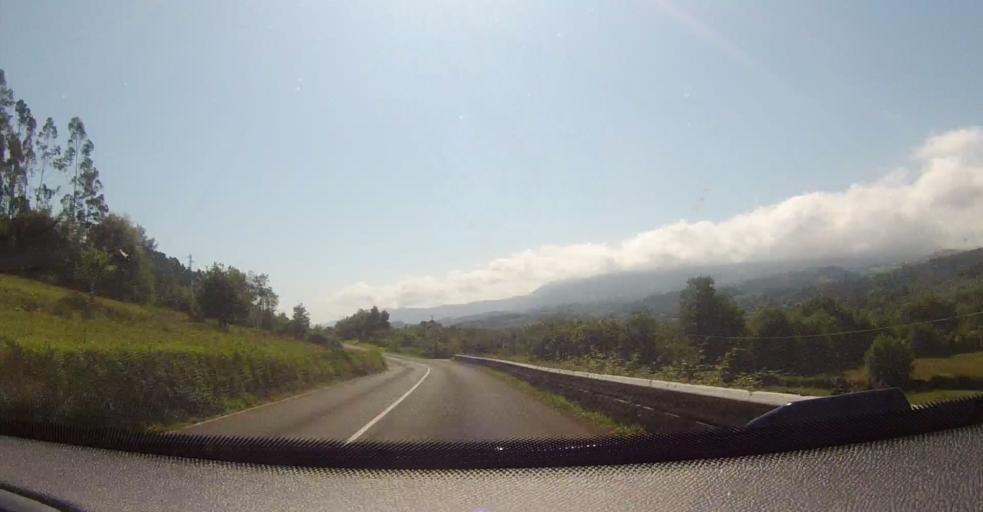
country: ES
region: Asturias
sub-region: Province of Asturias
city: Colunga
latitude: 43.4898
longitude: -5.3113
